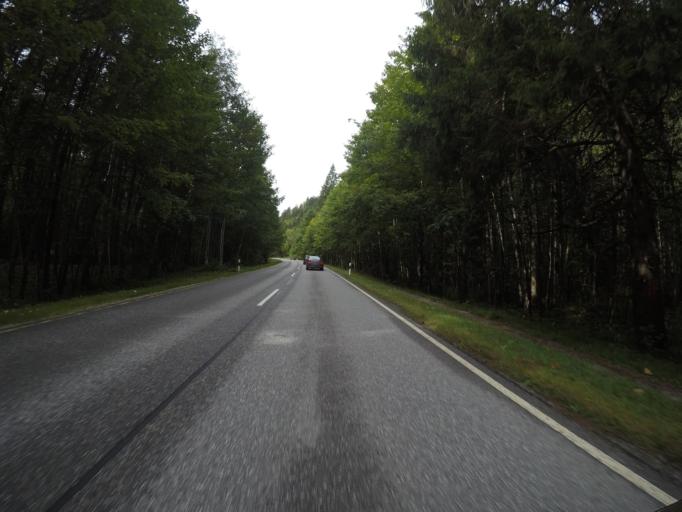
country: DE
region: Bavaria
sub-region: Upper Bavaria
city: Kreuth
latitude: 47.6154
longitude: 11.6733
